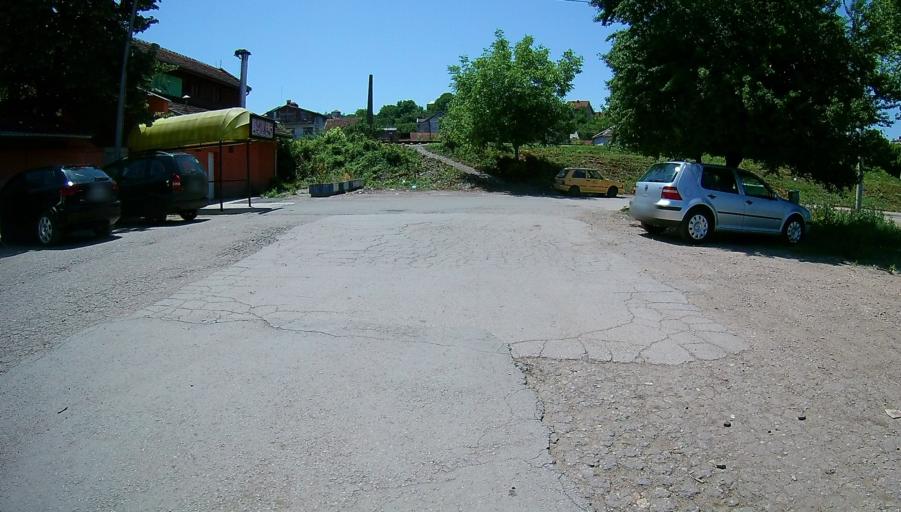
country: RS
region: Central Serbia
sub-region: Nisavski Okrug
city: Nis
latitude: 43.3129
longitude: 21.9050
